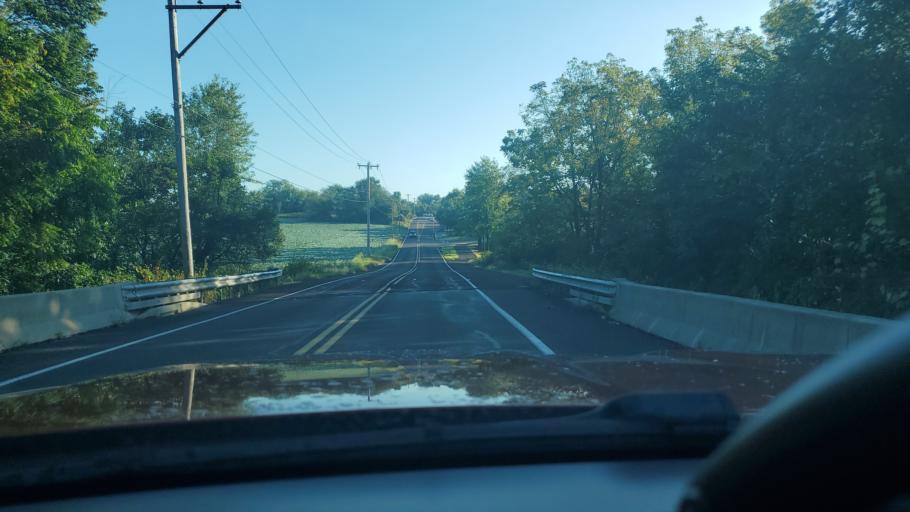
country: US
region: Pennsylvania
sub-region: Montgomery County
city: Woxall
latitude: 40.2974
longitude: -75.4170
